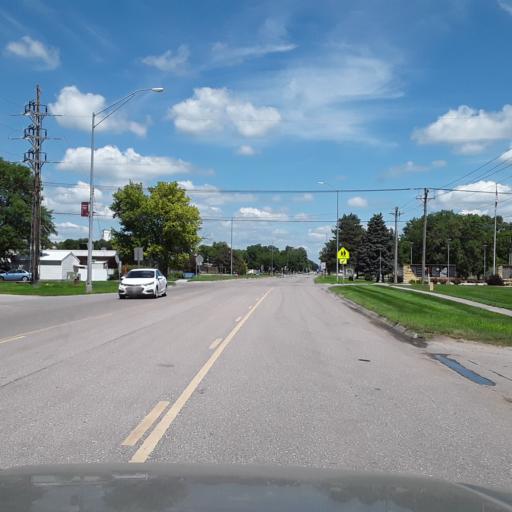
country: US
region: Nebraska
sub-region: Merrick County
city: Central City
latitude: 41.1041
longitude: -98.0017
